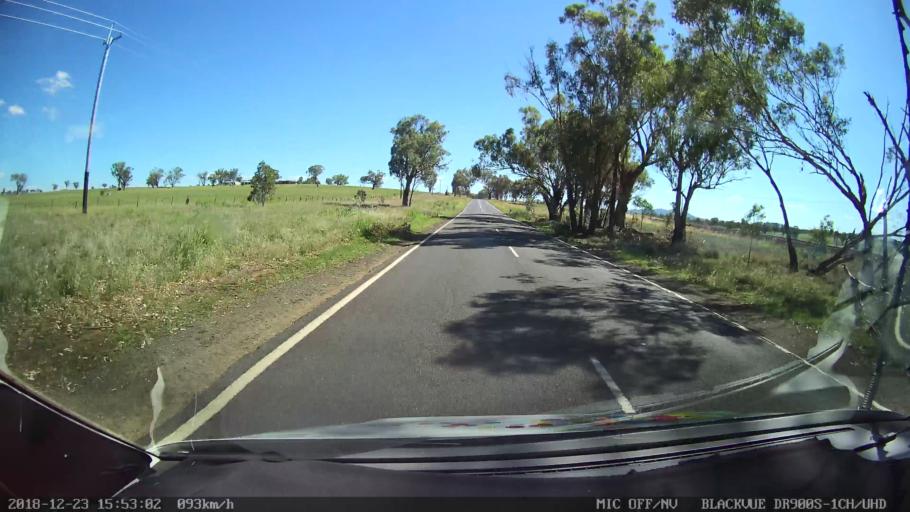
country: AU
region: New South Wales
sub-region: Tamworth Municipality
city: Phillip
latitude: -31.1283
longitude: 150.8842
